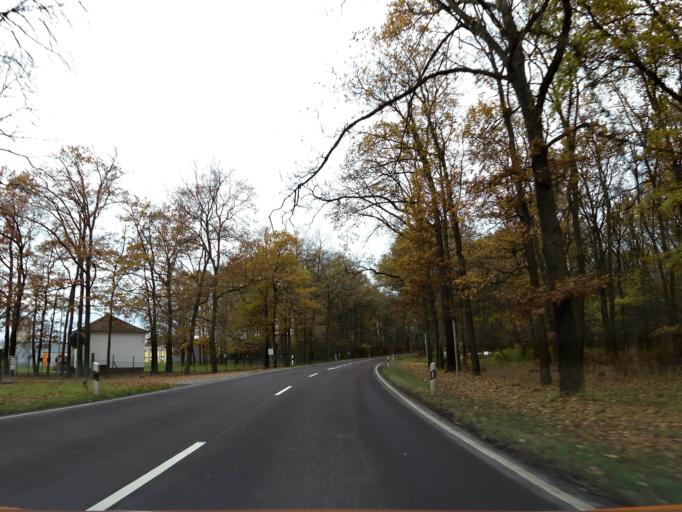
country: DE
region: Saxony-Anhalt
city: Haldensleben I
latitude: 52.3498
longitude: 11.4786
